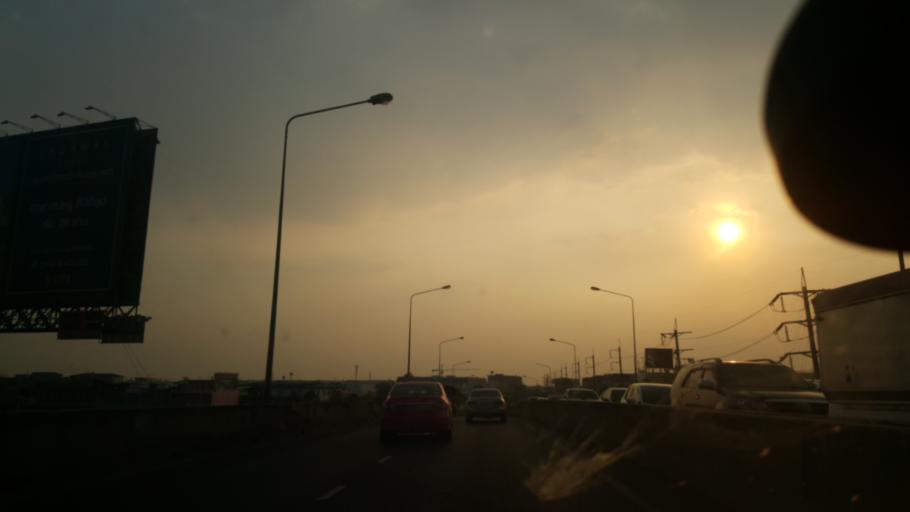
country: TH
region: Bangkok
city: Phasi Charoen
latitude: 13.6946
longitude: 100.4375
